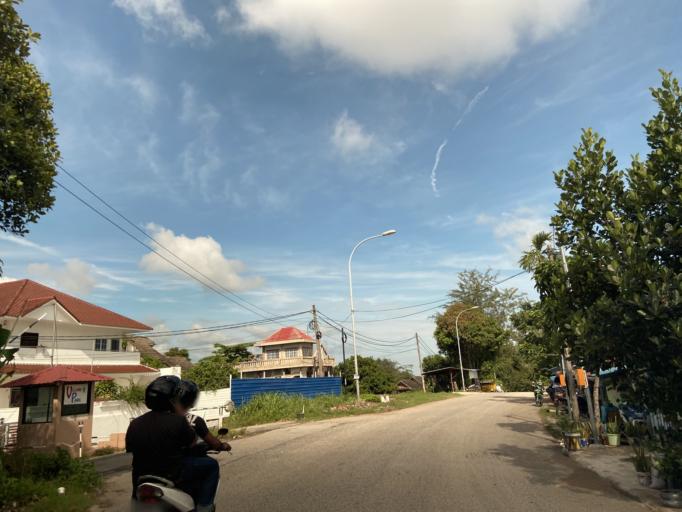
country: SG
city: Singapore
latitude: 1.1581
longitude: 104.0087
